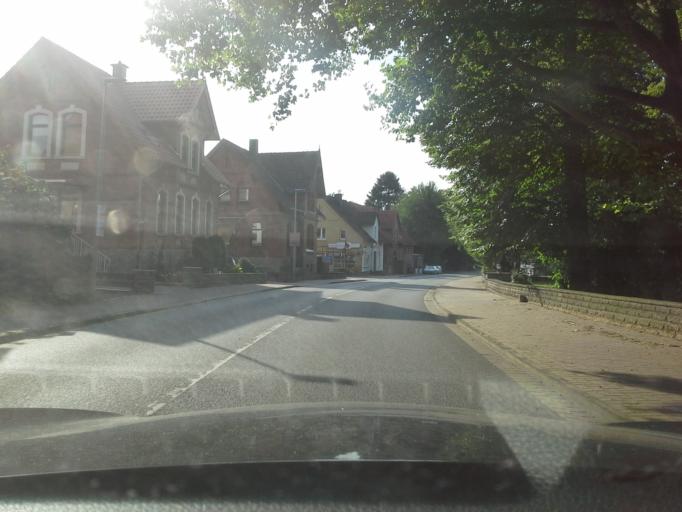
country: DE
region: Lower Saxony
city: Messenkamp
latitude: 52.2326
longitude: 9.4184
